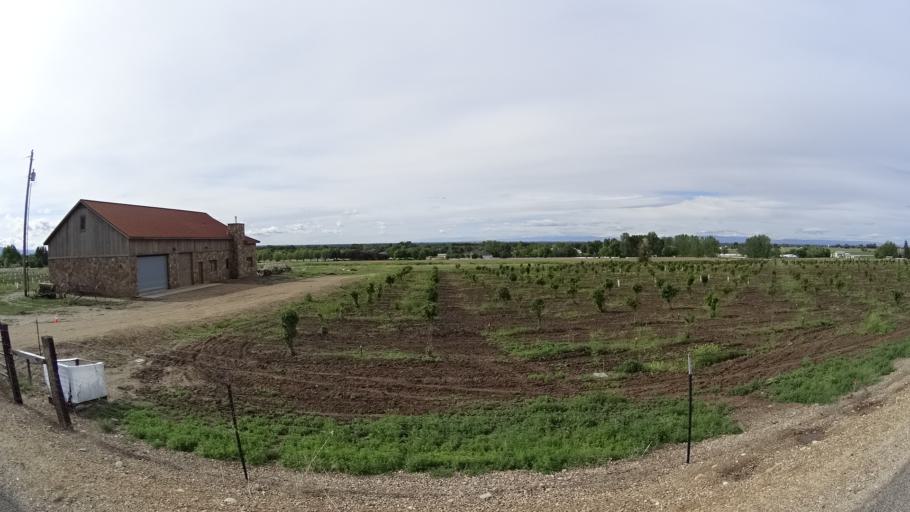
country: US
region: Idaho
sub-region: Ada County
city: Eagle
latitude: 43.7355
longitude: -116.4066
